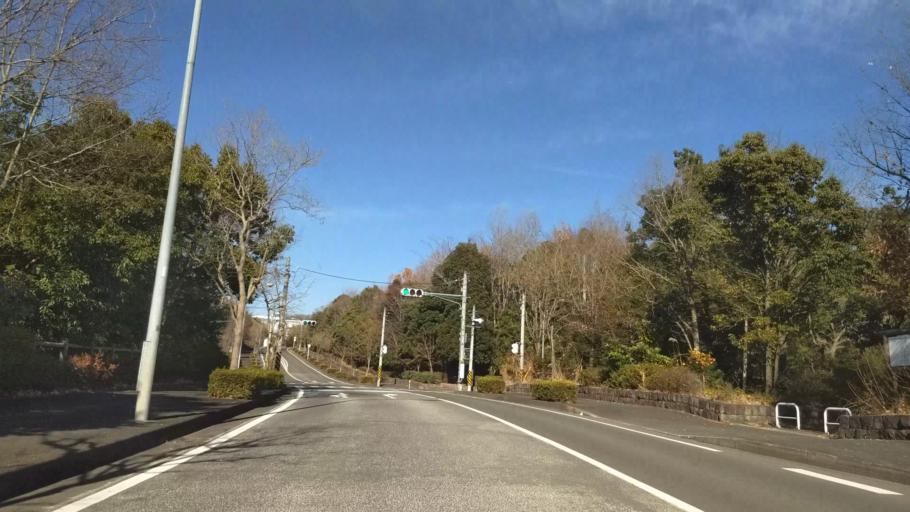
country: JP
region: Kanagawa
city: Hadano
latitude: 35.3442
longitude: 139.2221
